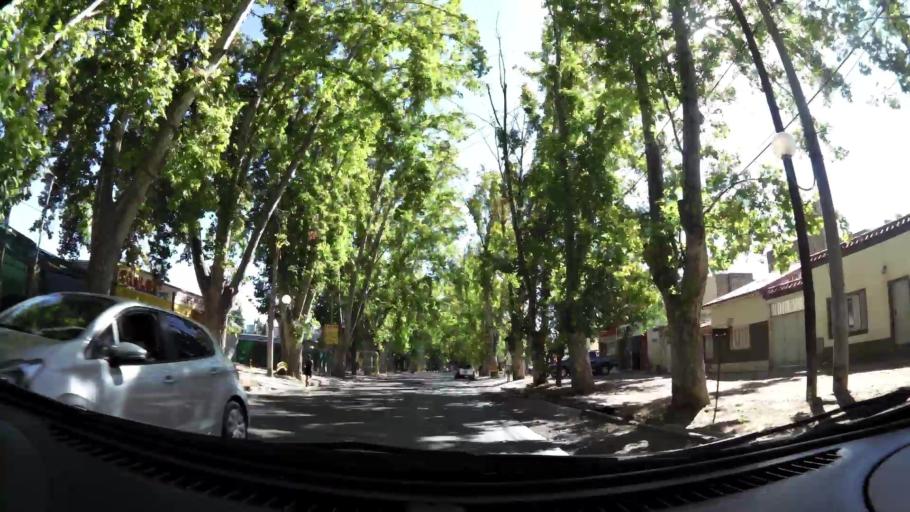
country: AR
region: Mendoza
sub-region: Departamento de Godoy Cruz
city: Godoy Cruz
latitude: -32.9775
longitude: -68.8579
